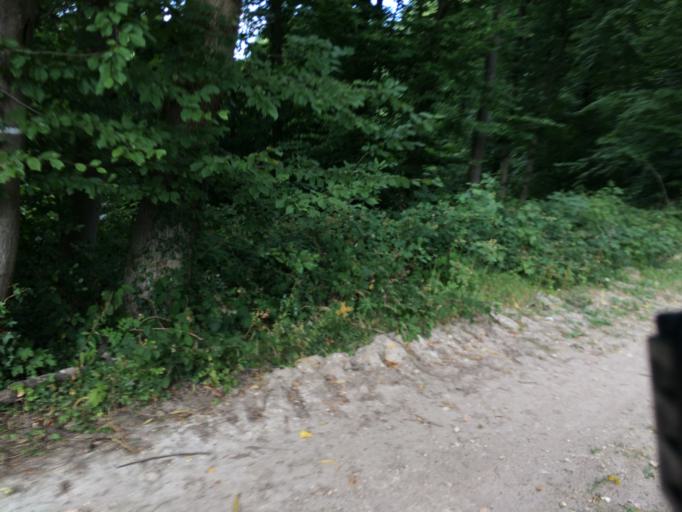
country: FR
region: Ile-de-France
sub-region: Departement de l'Essonne
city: Bievres
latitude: 48.7620
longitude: 2.2298
